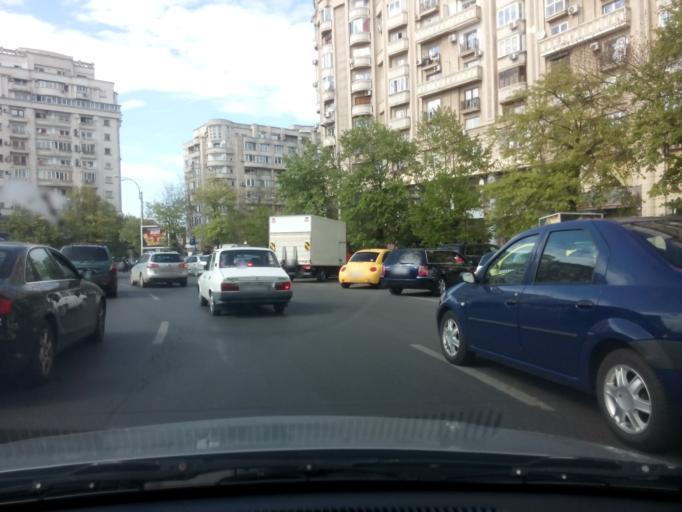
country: RO
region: Bucuresti
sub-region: Municipiul Bucuresti
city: Bucharest
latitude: 44.4257
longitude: 26.1299
